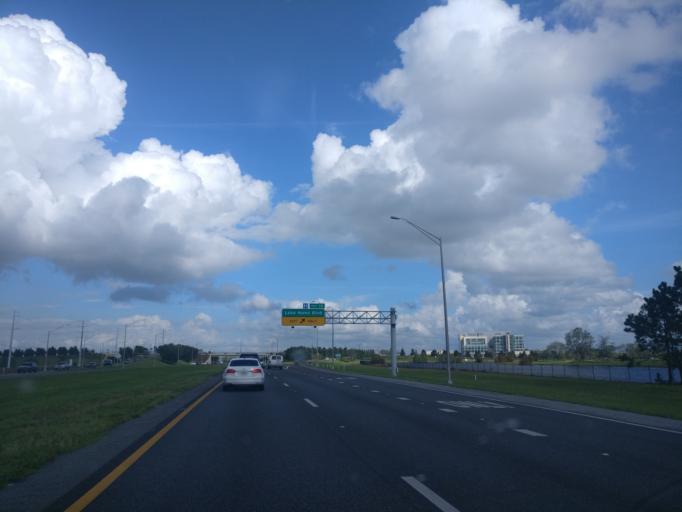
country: US
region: Florida
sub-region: Osceola County
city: Buenaventura Lakes
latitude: 28.3770
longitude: -81.2827
